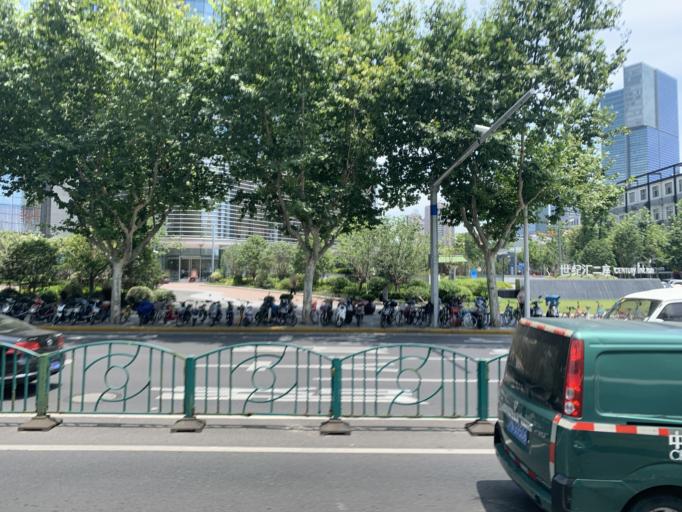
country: CN
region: Shanghai Shi
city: Pudong
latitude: 31.2283
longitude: 121.5221
